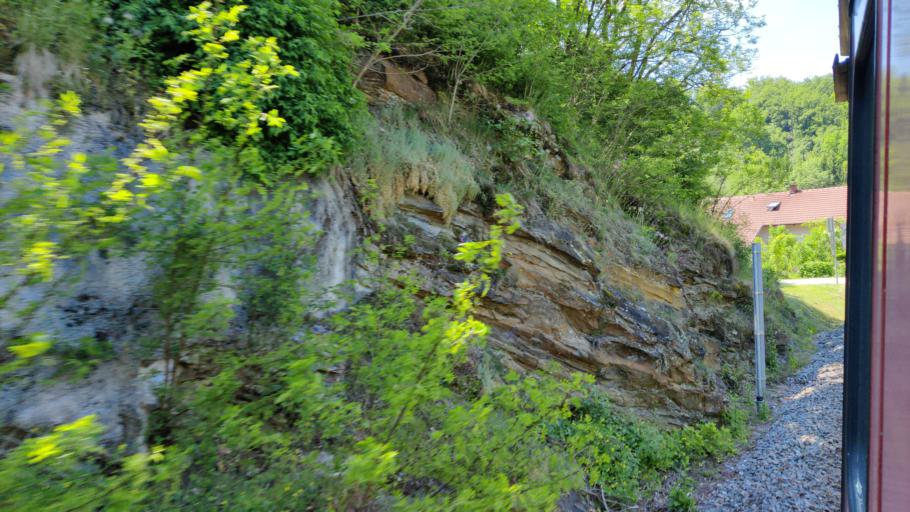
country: AT
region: Lower Austria
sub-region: Politischer Bezirk Horn
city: Horn
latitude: 48.6337
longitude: 15.6628
